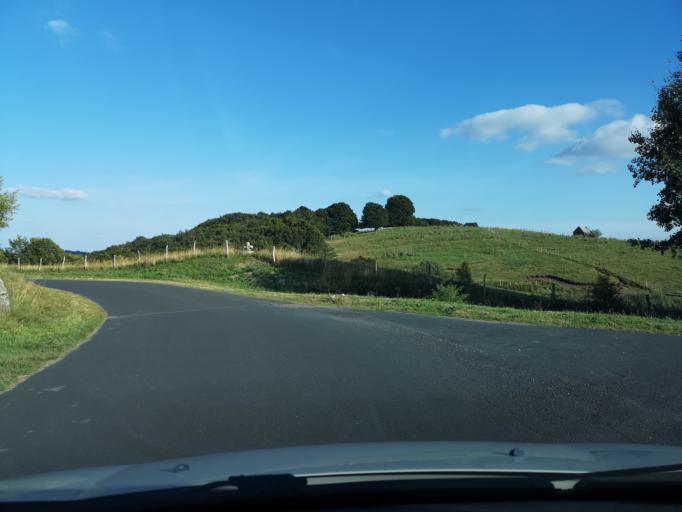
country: FR
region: Auvergne
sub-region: Departement du Puy-de-Dome
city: Mont-Dore
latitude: 45.4837
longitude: 2.9059
